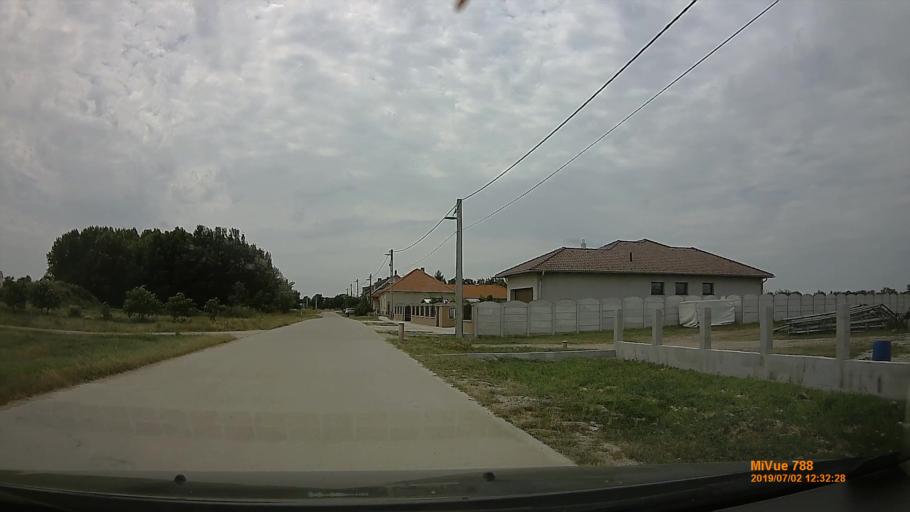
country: HU
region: Gyor-Moson-Sopron
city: Janossomorja
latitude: 47.8538
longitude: 17.1688
